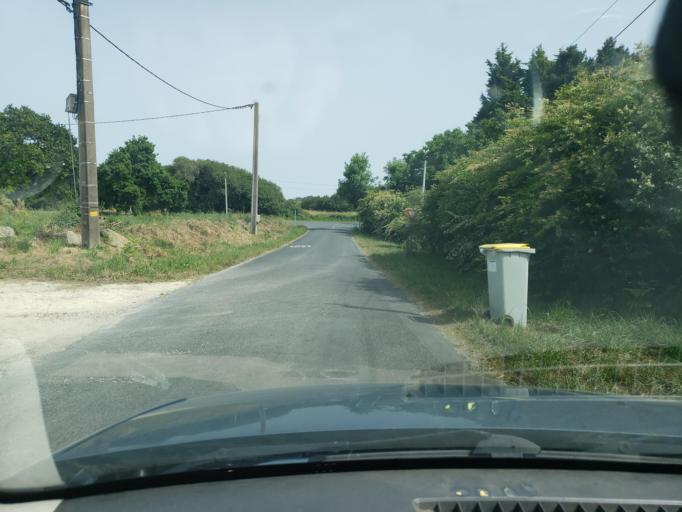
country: FR
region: Brittany
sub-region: Departement du Finistere
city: Plobannalec-Lesconil
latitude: 47.8158
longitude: -4.2390
